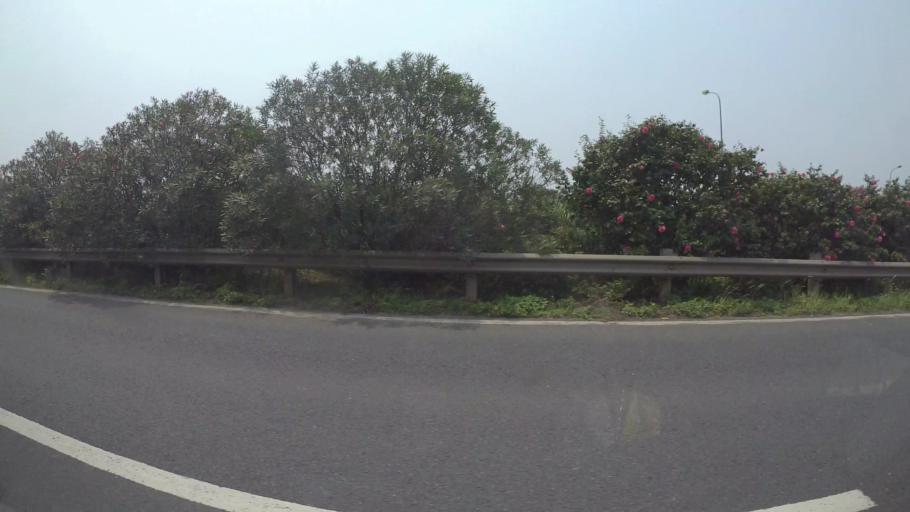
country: VN
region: Ha Noi
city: Quoc Oai
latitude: 21.0011
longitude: 105.6038
